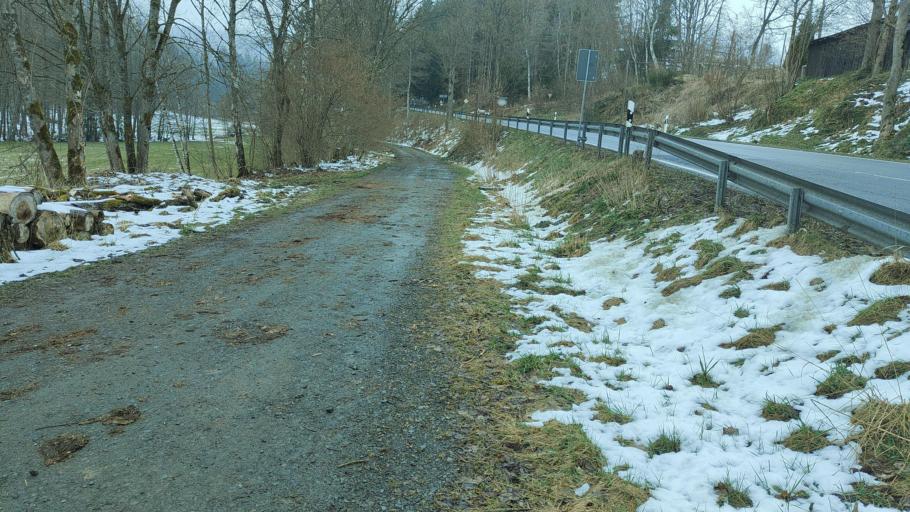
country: DE
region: North Rhine-Westphalia
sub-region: Regierungsbezirk Arnsberg
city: Bad Berleburg
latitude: 51.0969
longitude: 8.4339
